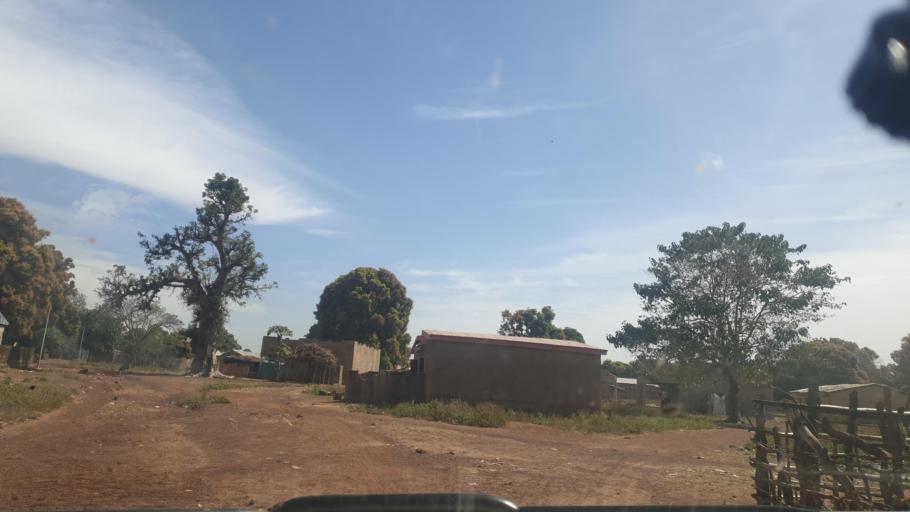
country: ML
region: Sikasso
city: Yanfolila
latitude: 10.4988
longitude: -7.9560
